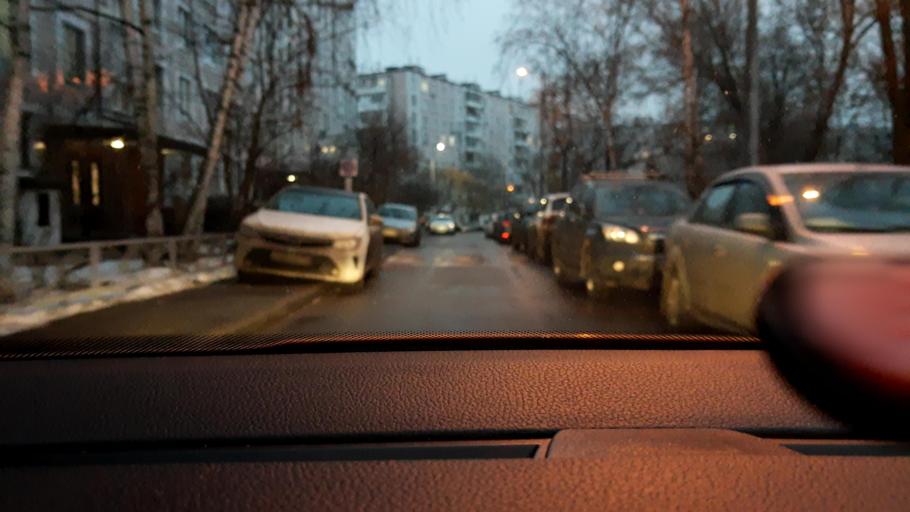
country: RU
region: Moscow
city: Strogino
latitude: 55.8073
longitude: 37.4000
